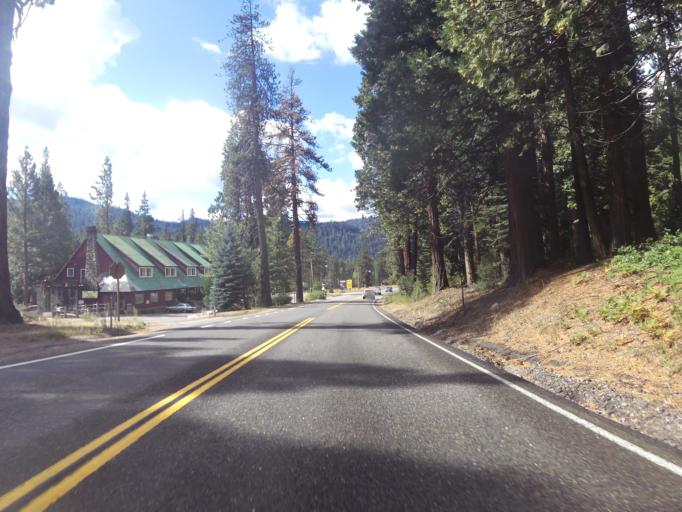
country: US
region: California
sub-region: El Dorado County
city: South Lake Tahoe
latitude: 38.7973
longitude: -120.1450
